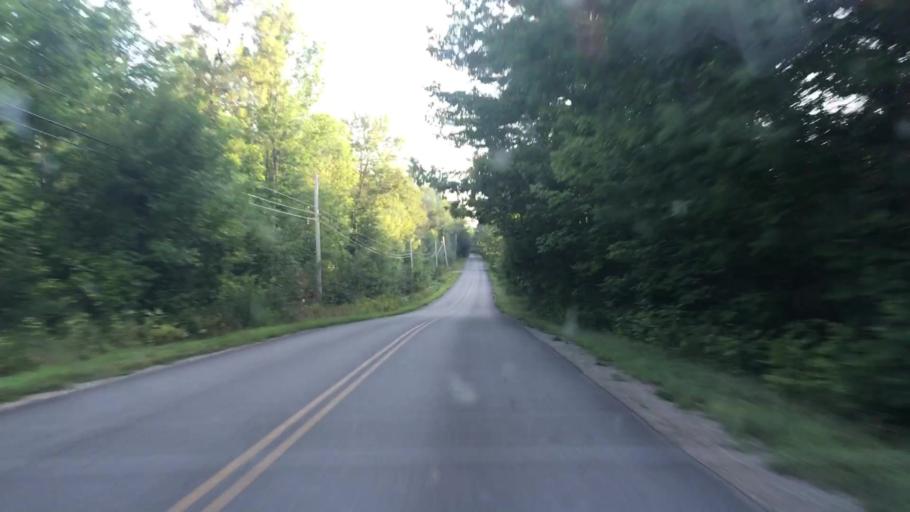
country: US
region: Maine
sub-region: Penobscot County
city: Hampden
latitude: 44.7043
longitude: -68.8901
